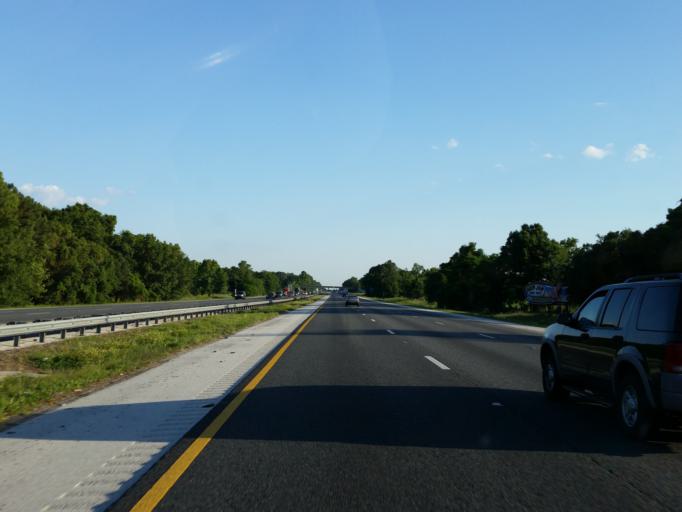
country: US
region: Florida
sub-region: Marion County
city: Ocala
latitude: 29.1299
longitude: -82.1849
